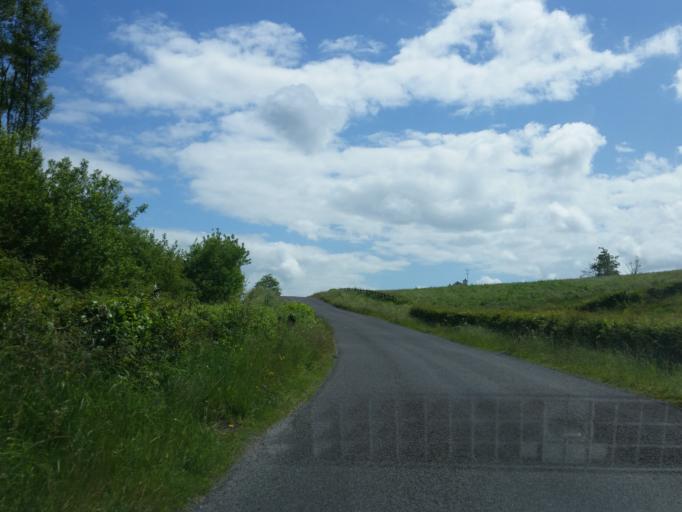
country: GB
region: Northern Ireland
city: Fivemiletown
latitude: 54.3536
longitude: -7.3006
